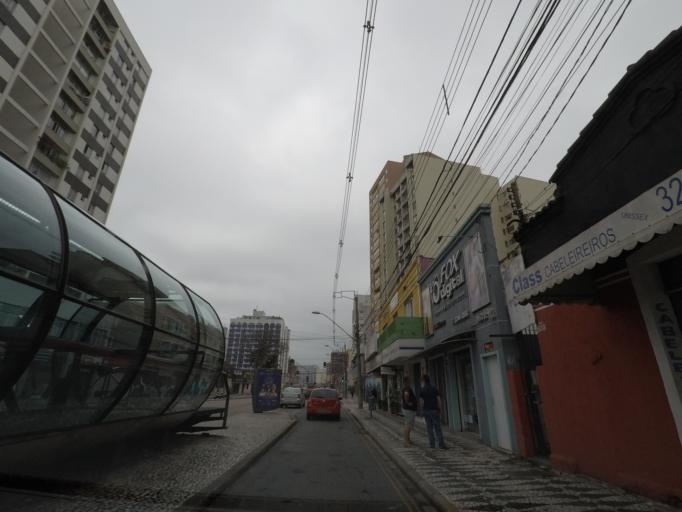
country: BR
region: Parana
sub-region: Curitiba
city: Curitiba
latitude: -25.4611
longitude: -49.2899
